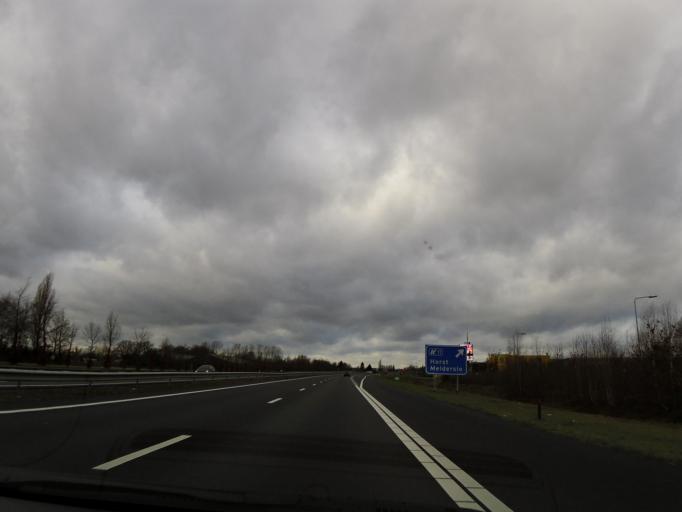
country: NL
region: Limburg
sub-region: Gemeente Peel en Maas
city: Maasbree
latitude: 51.4441
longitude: 6.0768
